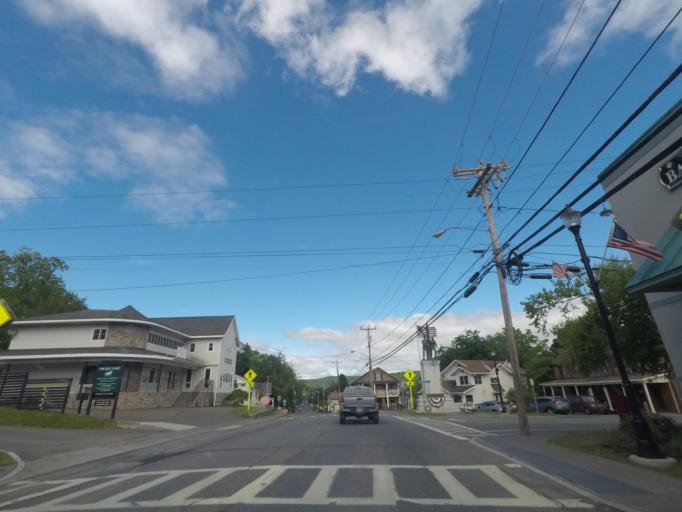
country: US
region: New York
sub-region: Columbia County
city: Philmont
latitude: 42.1791
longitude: -73.5260
